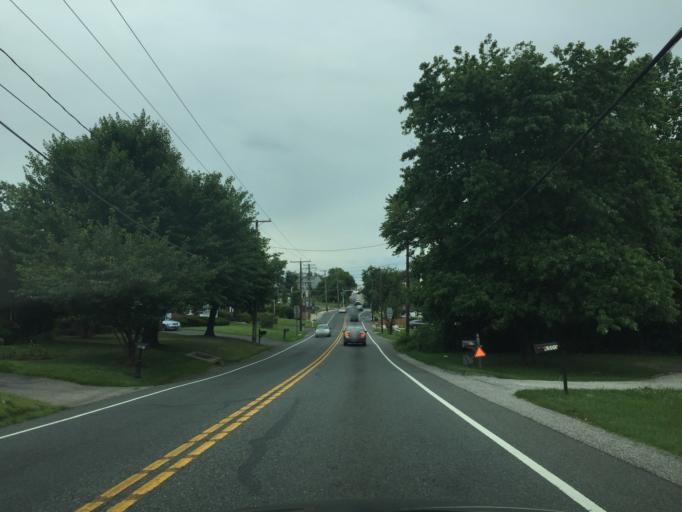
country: US
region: Maryland
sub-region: Baltimore County
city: Rosedale
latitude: 39.3371
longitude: -76.5028
